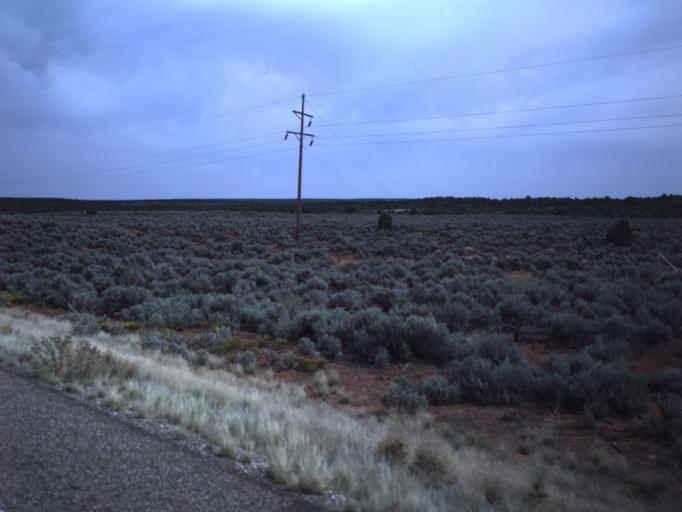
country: US
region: Utah
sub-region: Kane County
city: Kanab
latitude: 37.1232
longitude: -112.0998
